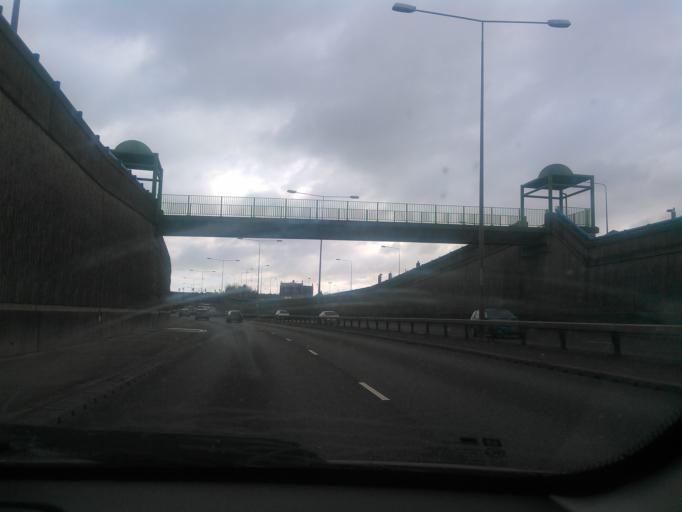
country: GB
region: England
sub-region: Staffordshire
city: Longton
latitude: 52.9864
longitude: -2.1378
